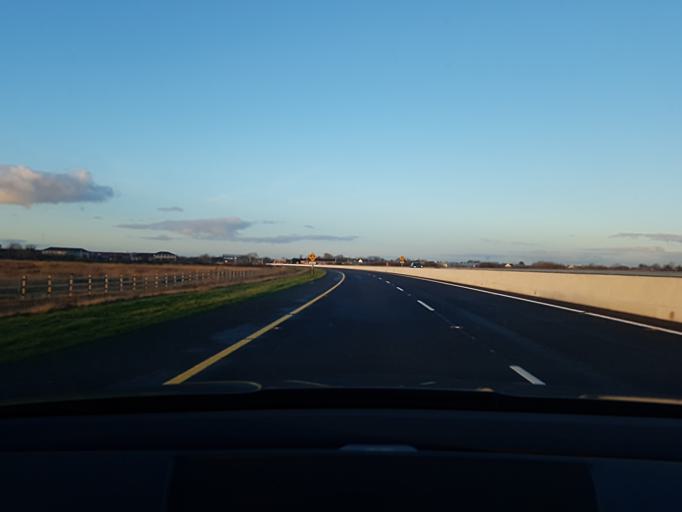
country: IE
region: Connaught
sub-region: County Galway
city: Tuam
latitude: 53.5028
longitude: -8.8781
